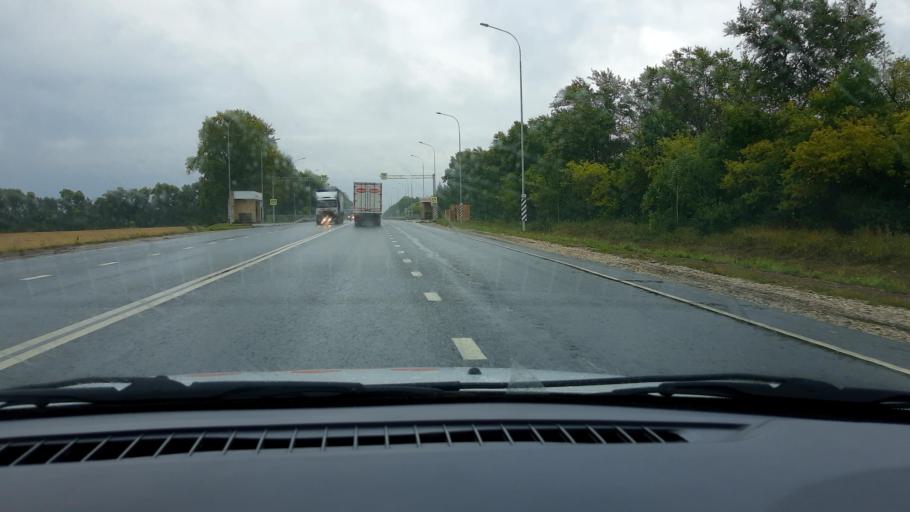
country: RU
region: Chuvashia
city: Yantikovo
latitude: 55.7899
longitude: 47.6894
